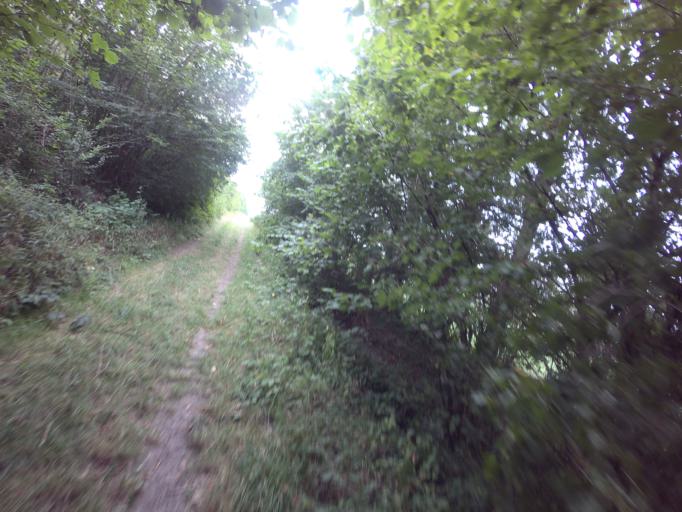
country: NL
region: Limburg
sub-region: Gemeente Simpelveld
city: Simpelveld
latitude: 50.7989
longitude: 5.9849
